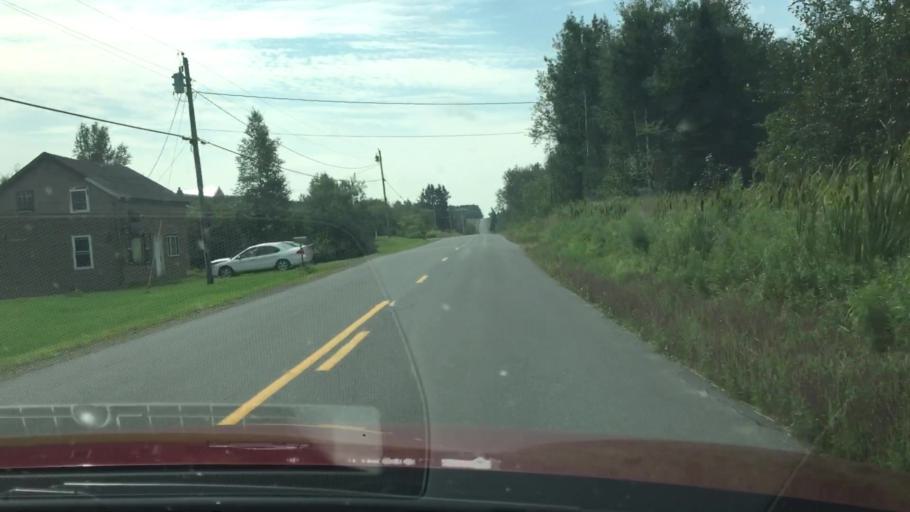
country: US
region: Maine
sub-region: Aroostook County
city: Caribou
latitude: 46.8143
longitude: -68.0246
